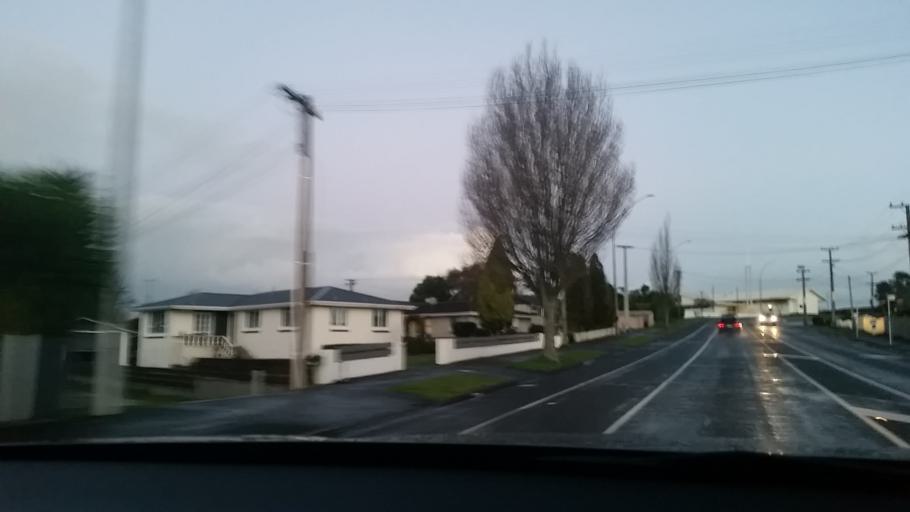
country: NZ
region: Waikato
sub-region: Hamilton City
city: Hamilton
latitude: -37.7979
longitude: 175.2477
